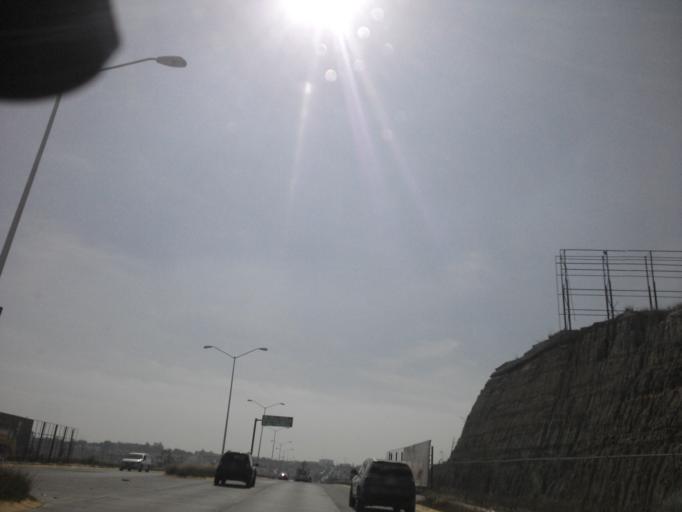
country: MX
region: Jalisco
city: Zapopan2
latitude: 20.7062
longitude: -103.4269
